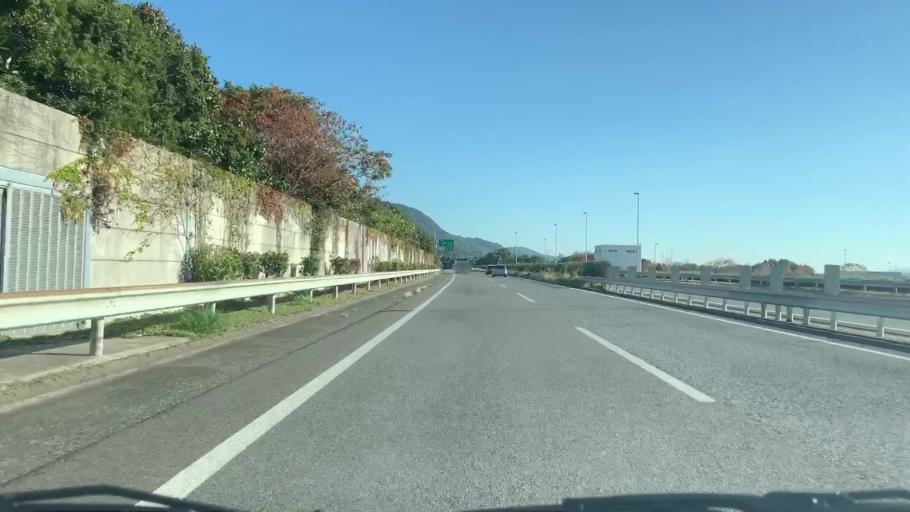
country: JP
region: Saga Prefecture
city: Saga-shi
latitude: 33.3203
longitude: 130.2747
